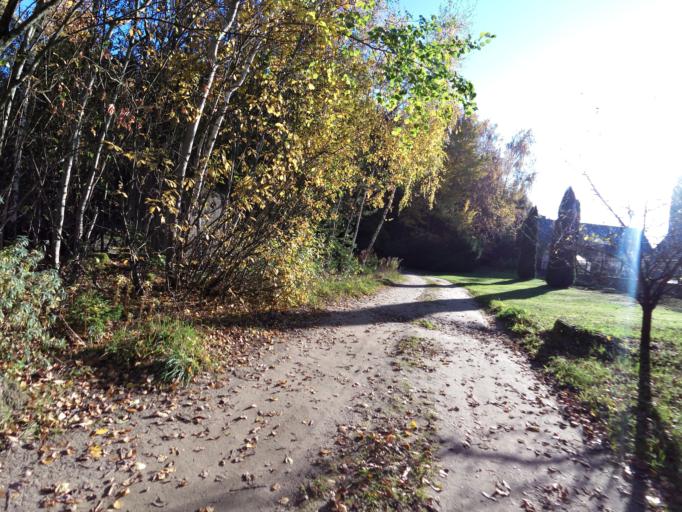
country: LT
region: Vilnius County
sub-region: Vilnius
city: Fabijoniskes
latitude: 54.7419
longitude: 25.2556
